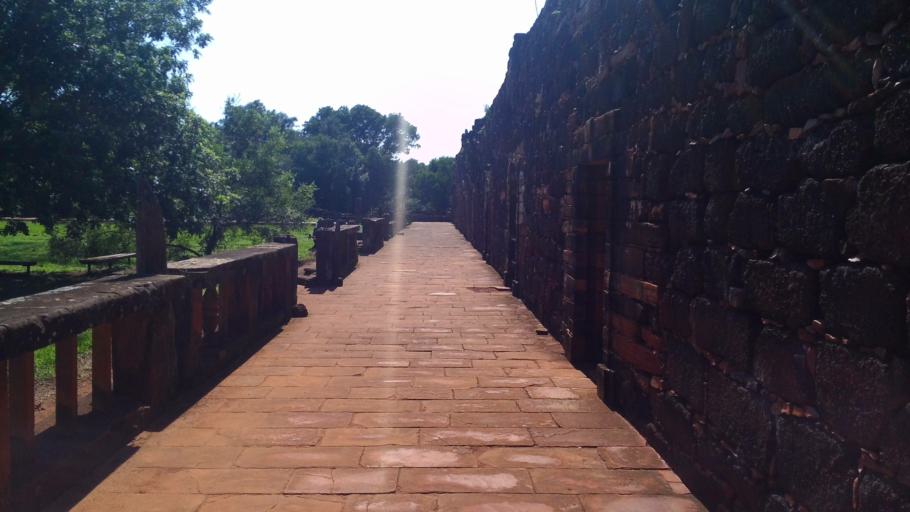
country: AR
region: Misiones
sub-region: Departamento de San Ignacio
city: San Ignacio
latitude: -27.2549
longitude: -55.5316
